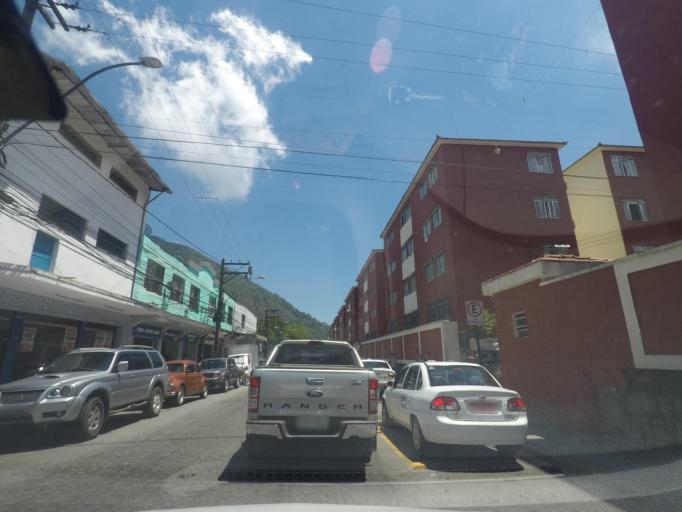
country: BR
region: Rio de Janeiro
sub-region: Petropolis
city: Petropolis
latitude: -22.5296
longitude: -43.1722
